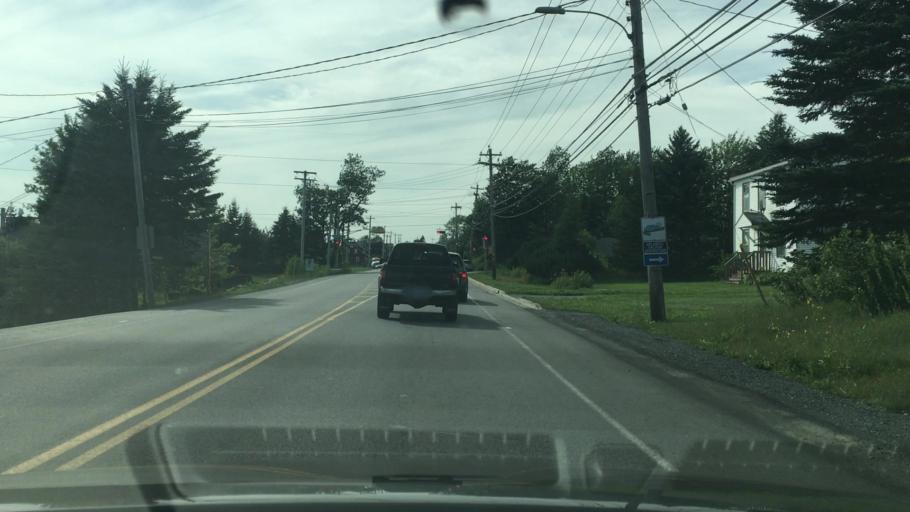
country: CA
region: Nova Scotia
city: Dartmouth
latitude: 44.7320
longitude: -63.7581
